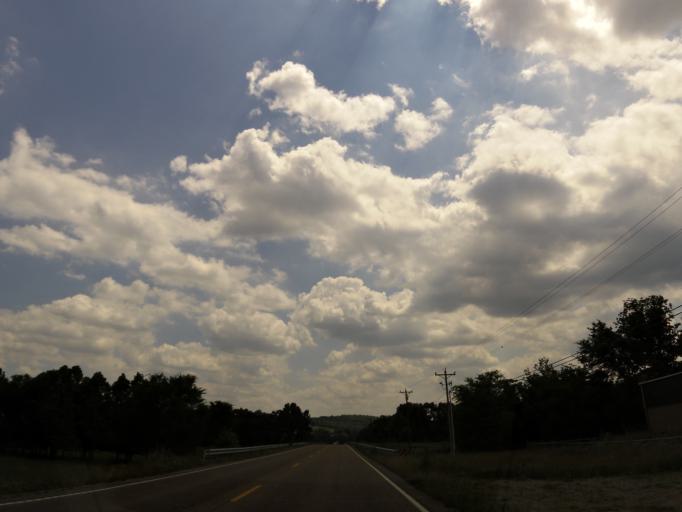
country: US
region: Tennessee
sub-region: Bledsoe County
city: Pikeville
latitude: 35.5483
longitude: -85.2547
